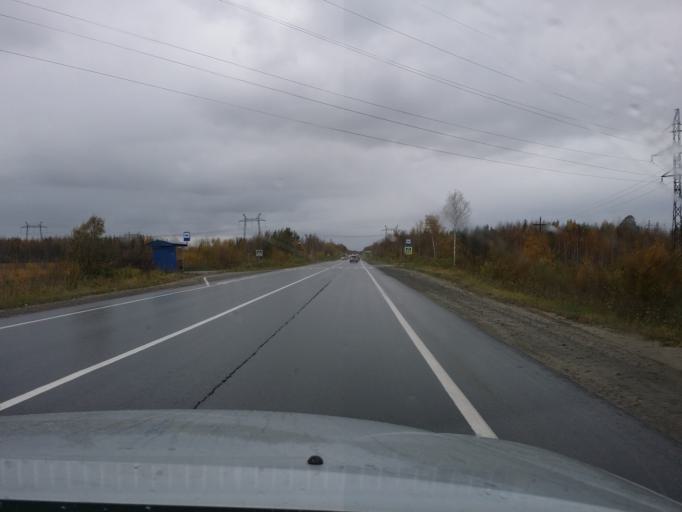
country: RU
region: Khanty-Mansiyskiy Avtonomnyy Okrug
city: Megion
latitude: 61.0870
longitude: 76.1084
